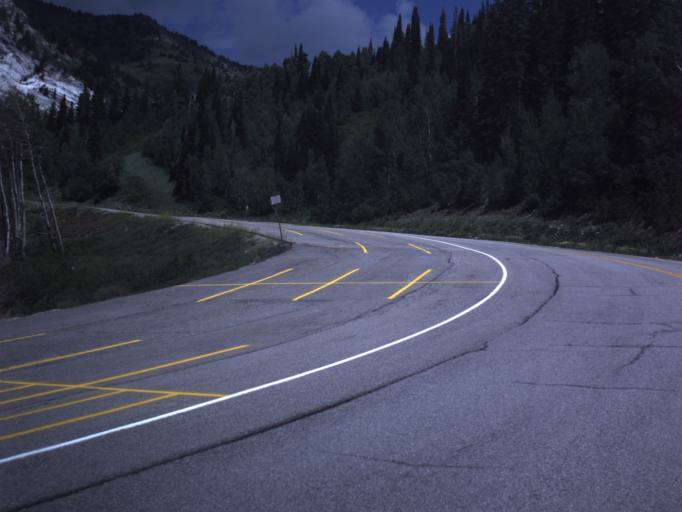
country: US
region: Utah
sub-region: Salt Lake County
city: Granite
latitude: 40.5818
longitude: -111.6511
